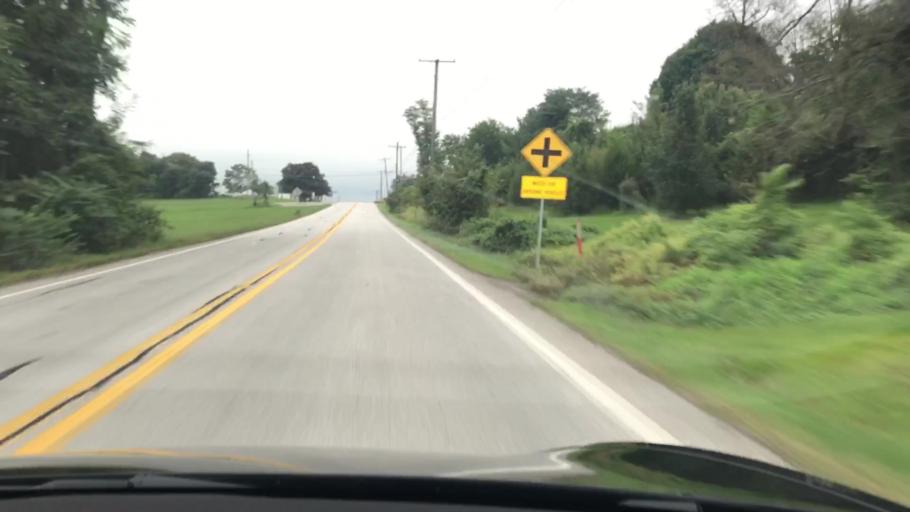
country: US
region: Pennsylvania
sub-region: Adams County
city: Lake Meade
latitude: 39.9357
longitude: -77.0491
